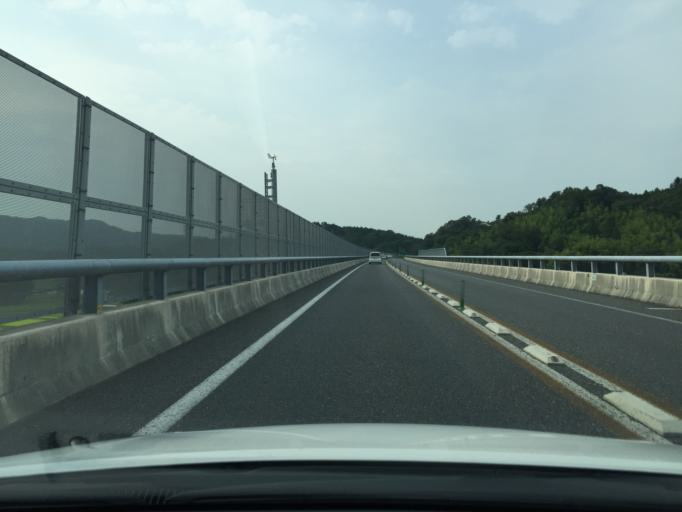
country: JP
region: Fukushima
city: Iwaki
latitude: 37.2157
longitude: 140.9786
